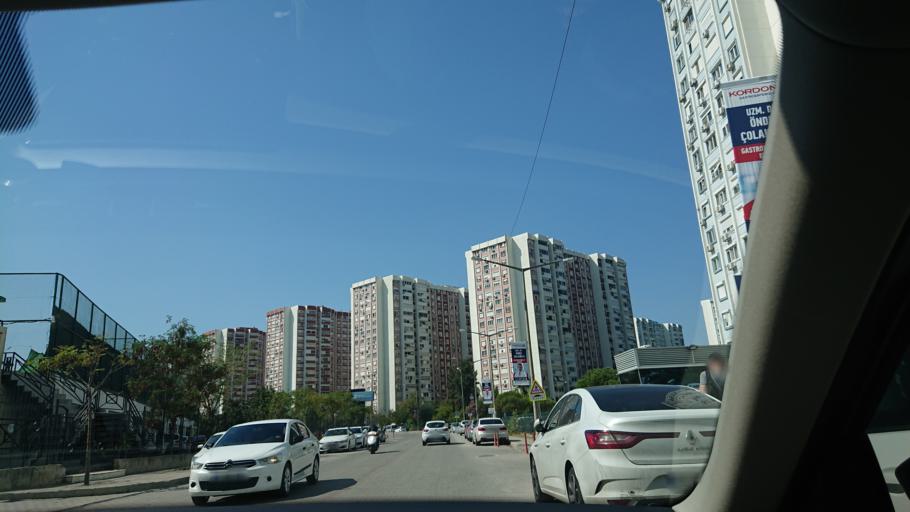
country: TR
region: Izmir
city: Karsiyaka
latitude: 38.4686
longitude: 27.0807
